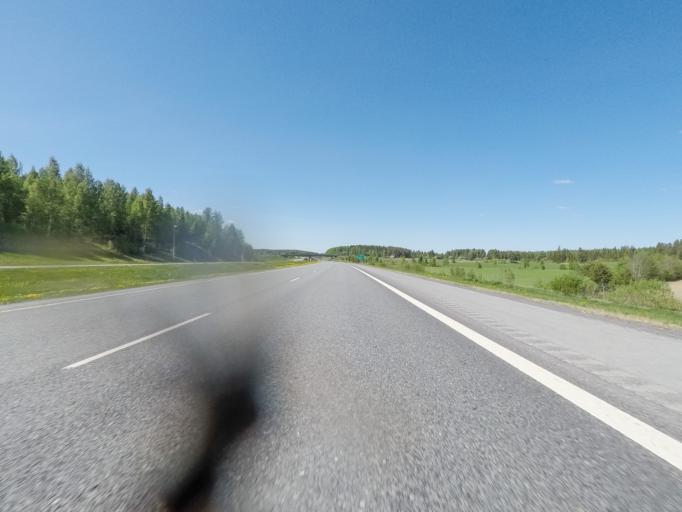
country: FI
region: Pirkanmaa
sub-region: Etelae-Pirkanmaa
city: Akaa
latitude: 61.1631
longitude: 23.9584
